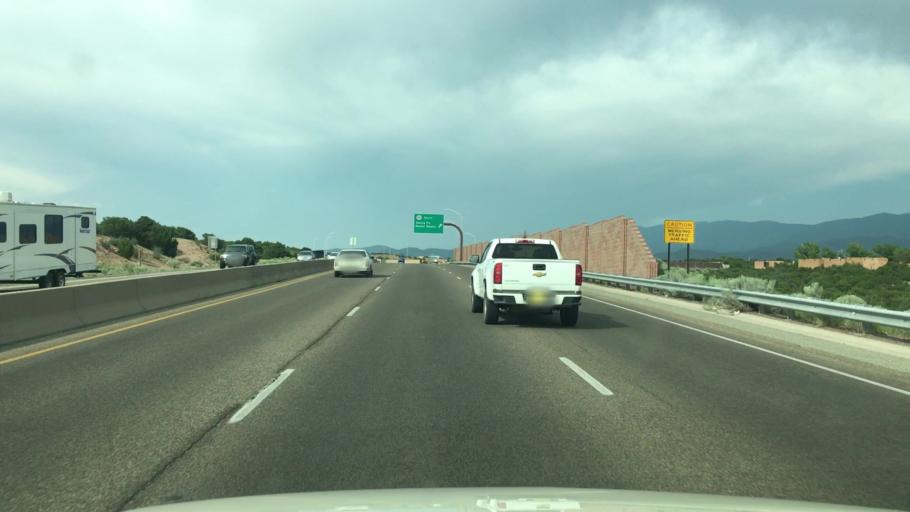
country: US
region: New Mexico
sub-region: Santa Fe County
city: Santa Fe
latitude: 35.7056
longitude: -105.9442
